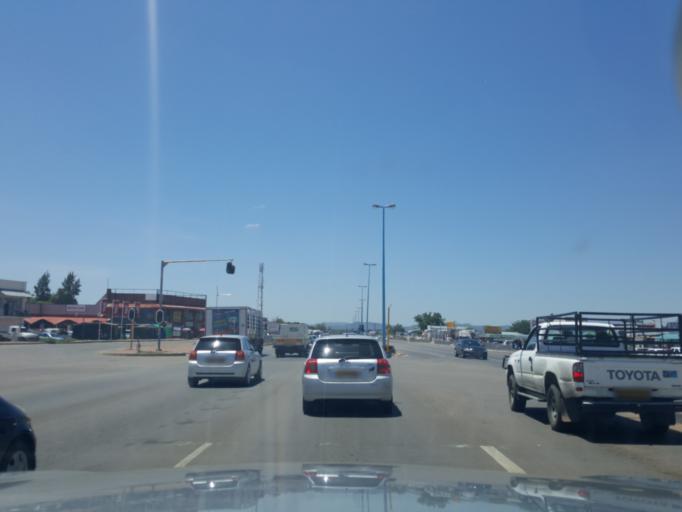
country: BW
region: Kweneng
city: Mogoditshane
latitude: -24.6216
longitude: 25.8672
